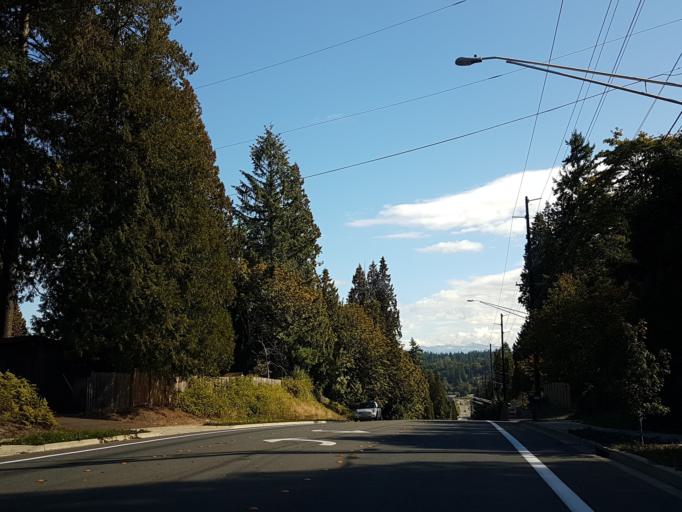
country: US
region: Washington
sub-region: Snohomish County
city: North Creek
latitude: 47.7906
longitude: -122.1599
